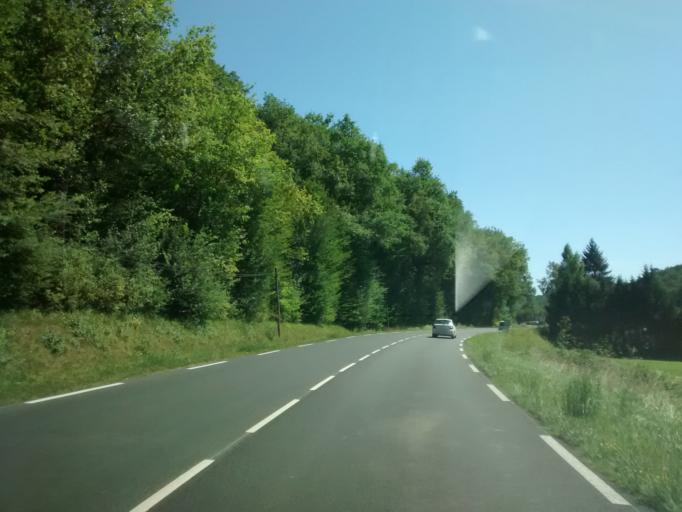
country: FR
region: Aquitaine
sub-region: Departement de la Dordogne
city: Boulazac
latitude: 45.1083
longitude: 0.8350
